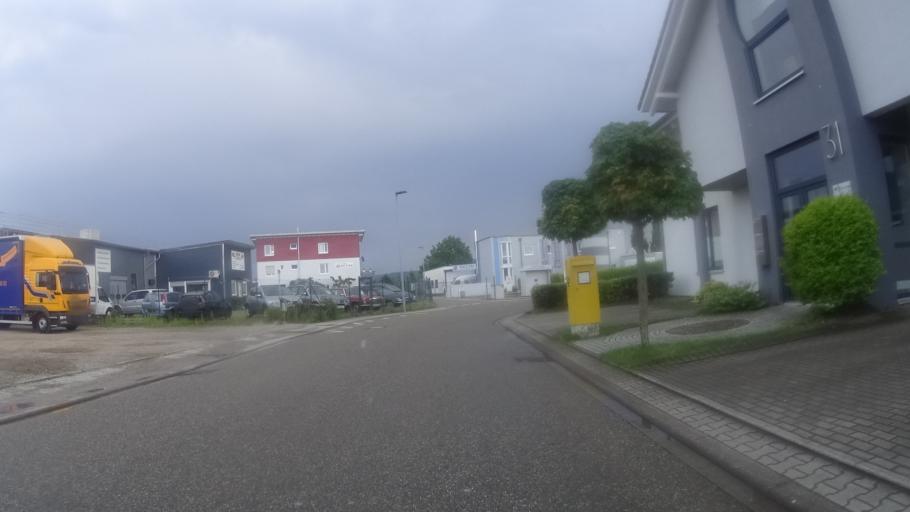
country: DE
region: Baden-Wuerttemberg
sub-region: Karlsruhe Region
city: Otigheim
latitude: 48.8878
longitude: 8.2430
